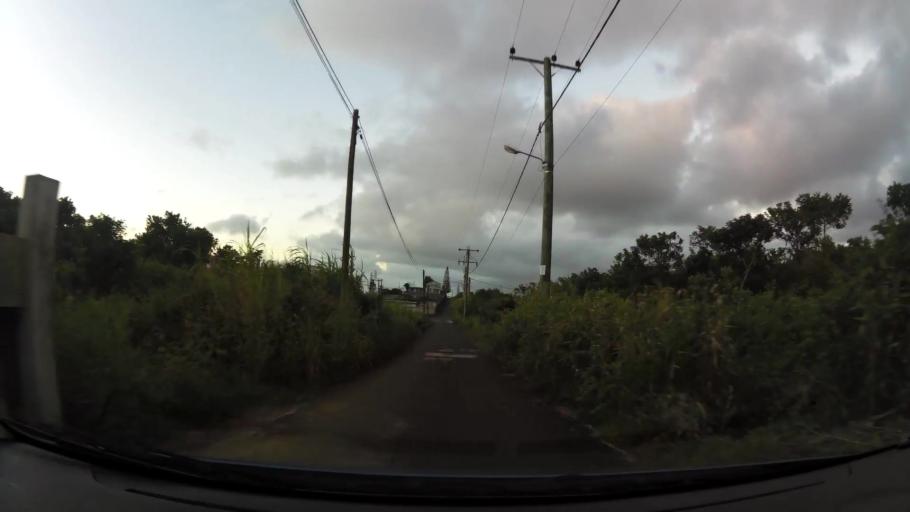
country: MU
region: Plaines Wilhems
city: Curepipe
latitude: -20.2981
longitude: 57.5307
